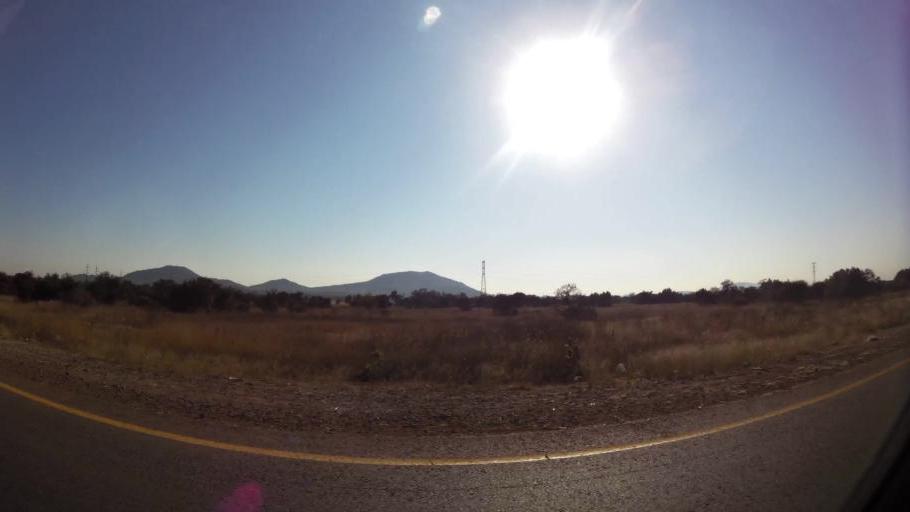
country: ZA
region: Gauteng
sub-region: City of Tshwane Metropolitan Municipality
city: Pretoria
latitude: -25.6503
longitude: 28.1582
